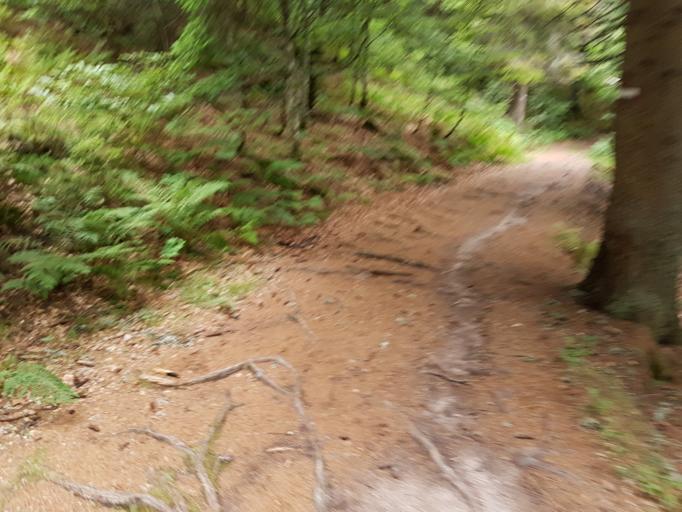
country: FR
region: Alsace
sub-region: Departement du Haut-Rhin
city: Soultzeren
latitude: 48.0897
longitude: 7.0597
